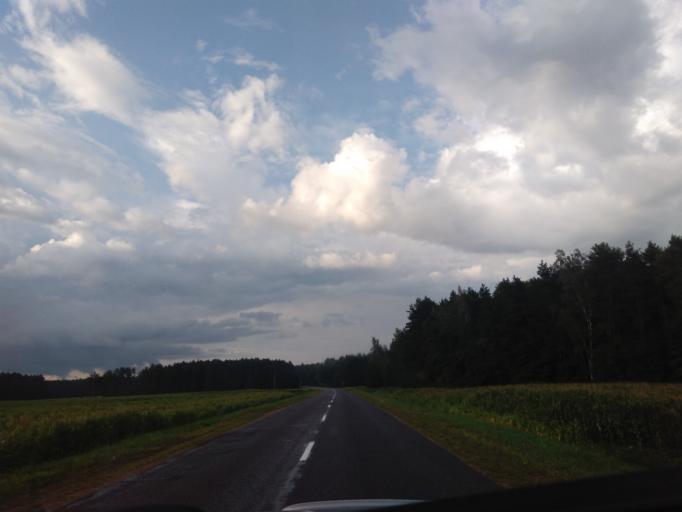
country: BY
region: Minsk
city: Uzda
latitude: 53.3521
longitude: 27.0963
